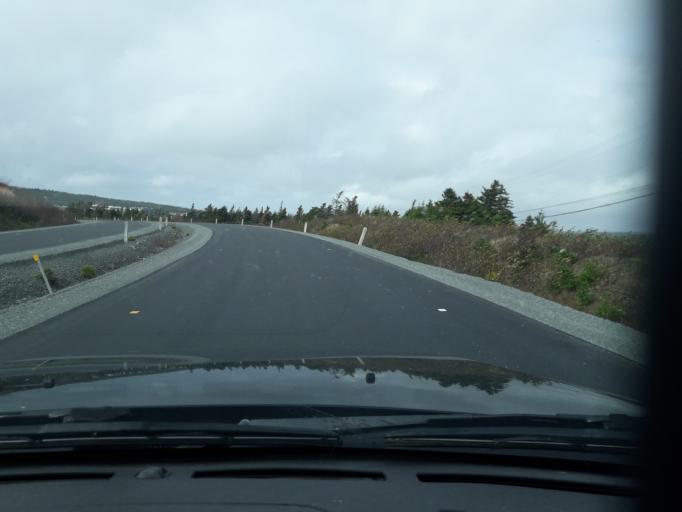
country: CA
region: Newfoundland and Labrador
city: Mount Pearl
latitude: 47.5549
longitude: -52.7712
